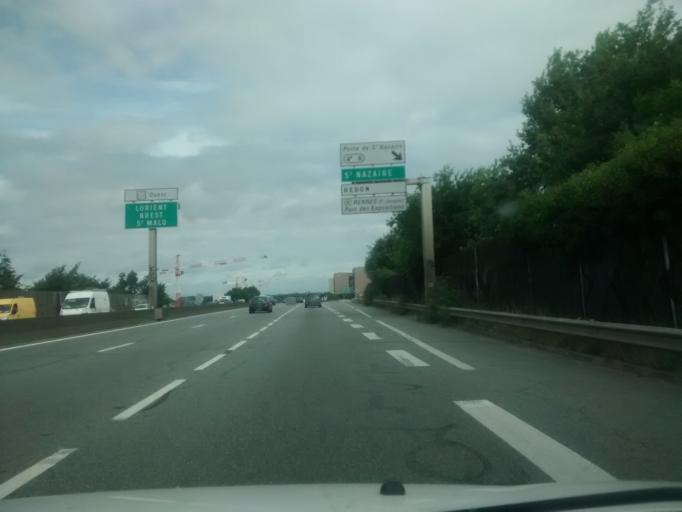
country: FR
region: Brittany
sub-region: Departement d'Ille-et-Vilaine
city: Saint-Jacques-de-la-Lande
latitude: 48.0880
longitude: -1.7017
